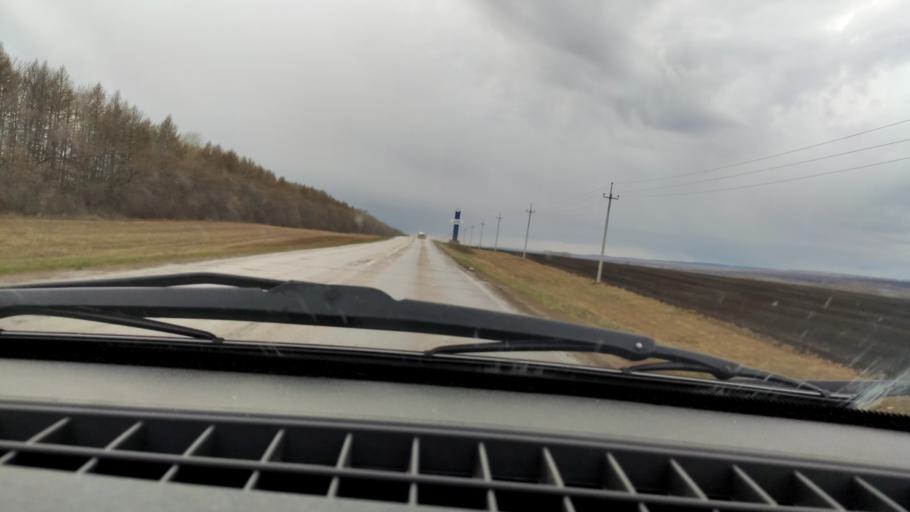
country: RU
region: Bashkortostan
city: Chekmagush
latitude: 55.1100
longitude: 54.9363
